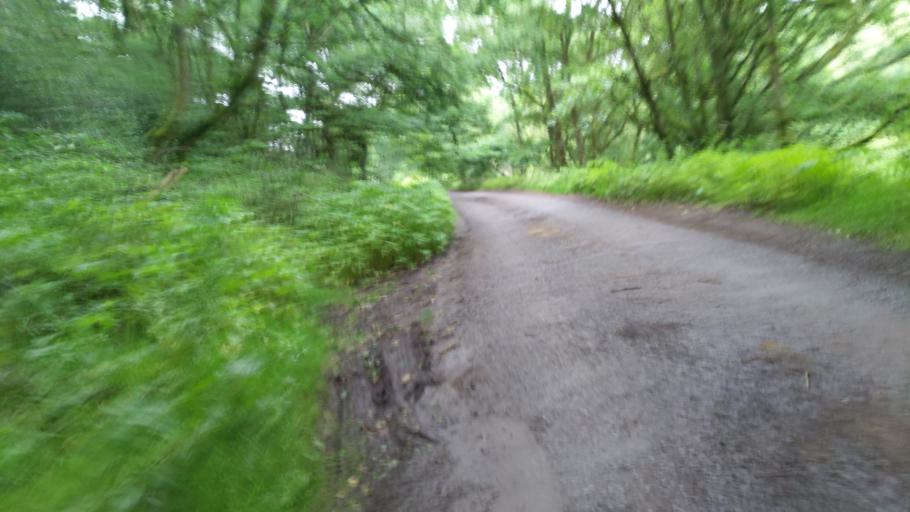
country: GB
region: England
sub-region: Lancashire
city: Chorley
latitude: 53.6778
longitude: -2.5844
